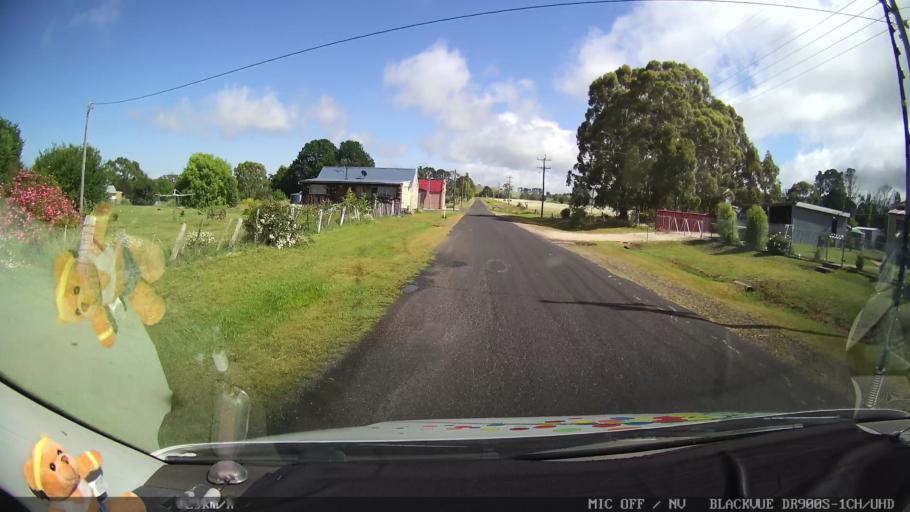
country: AU
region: New South Wales
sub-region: Guyra
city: Guyra
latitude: -30.0204
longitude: 151.6590
